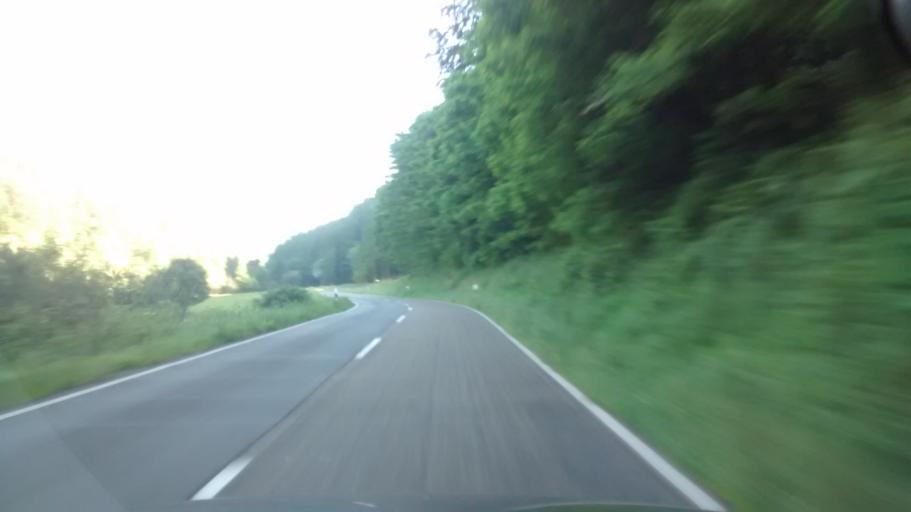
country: DE
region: Rheinland-Pfalz
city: Niederschlettenbach
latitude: 49.1002
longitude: 7.8498
